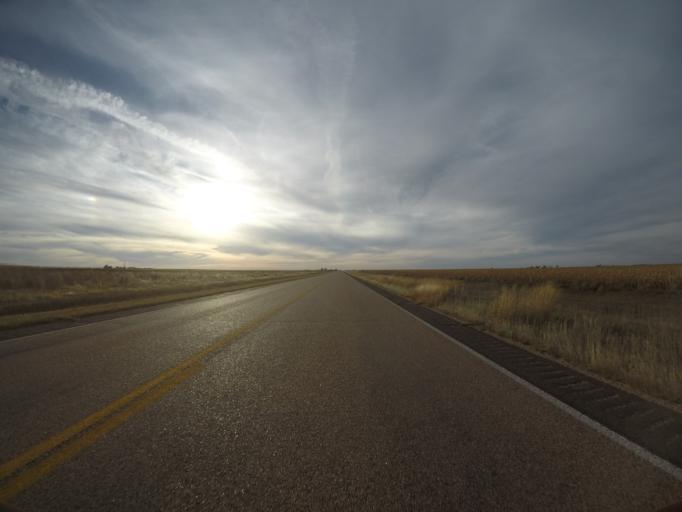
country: US
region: Colorado
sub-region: Kit Carson County
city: Burlington
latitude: 39.6563
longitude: -102.6001
